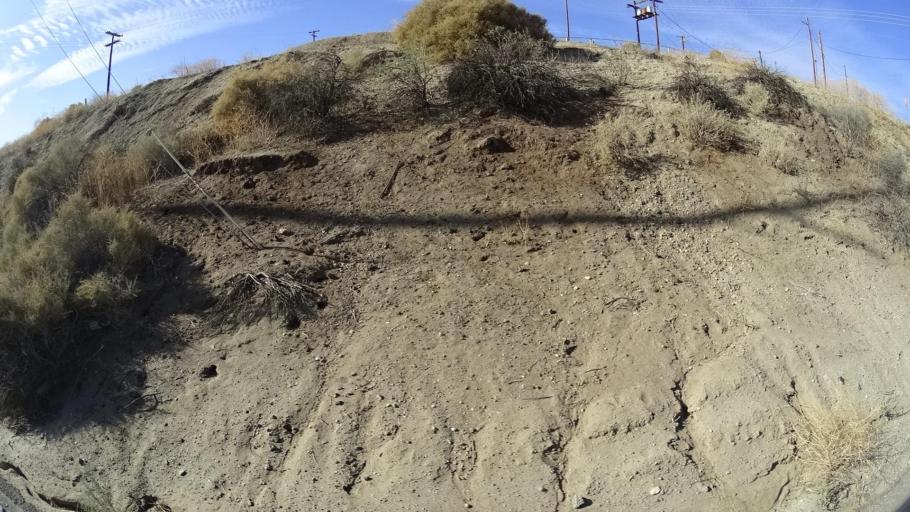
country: US
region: California
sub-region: Kern County
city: Oildale
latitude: 35.5806
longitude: -118.9593
